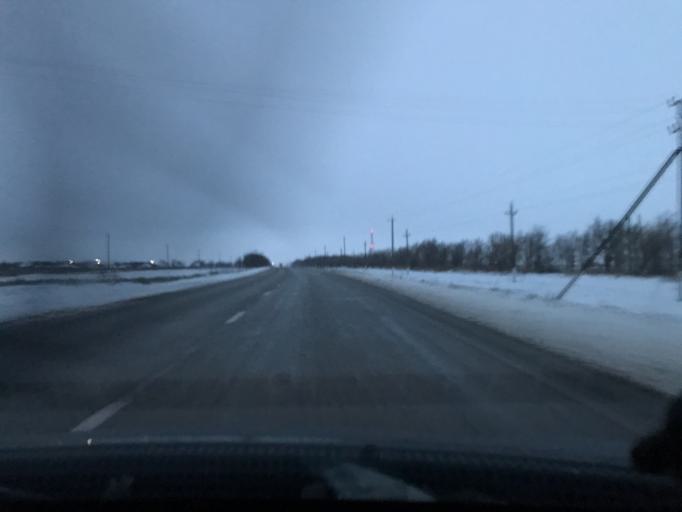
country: RU
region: Rostov
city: Letnik
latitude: 45.9134
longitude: 41.2916
